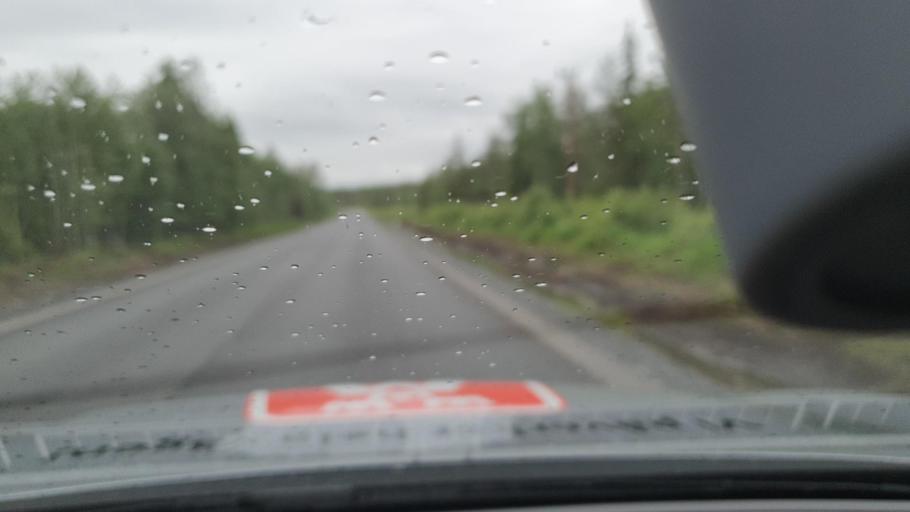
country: SE
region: Norrbotten
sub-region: Overkalix Kommun
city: OEverkalix
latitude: 66.7017
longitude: 23.2035
